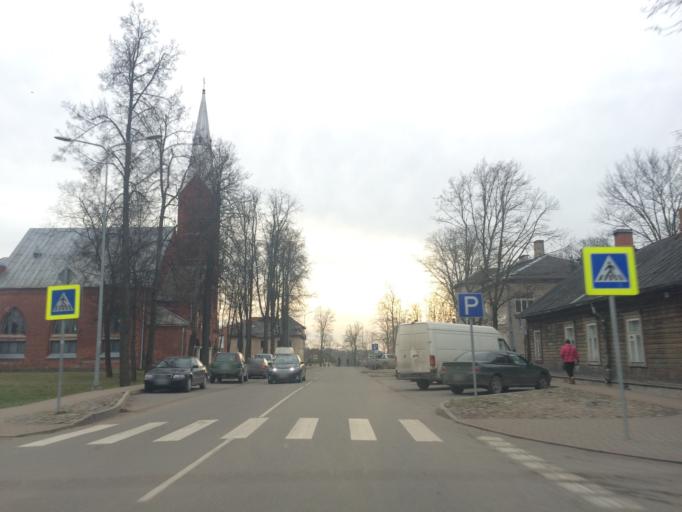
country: LV
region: Rezekne
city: Rezekne
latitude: 56.5064
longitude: 27.3370
